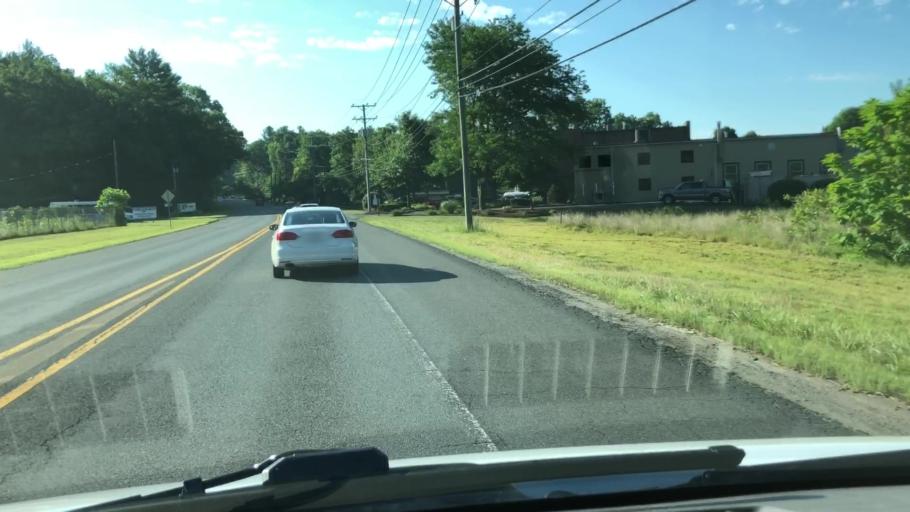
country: US
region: Massachusetts
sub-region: Hampshire County
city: North Amherst
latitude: 42.4502
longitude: -72.5608
